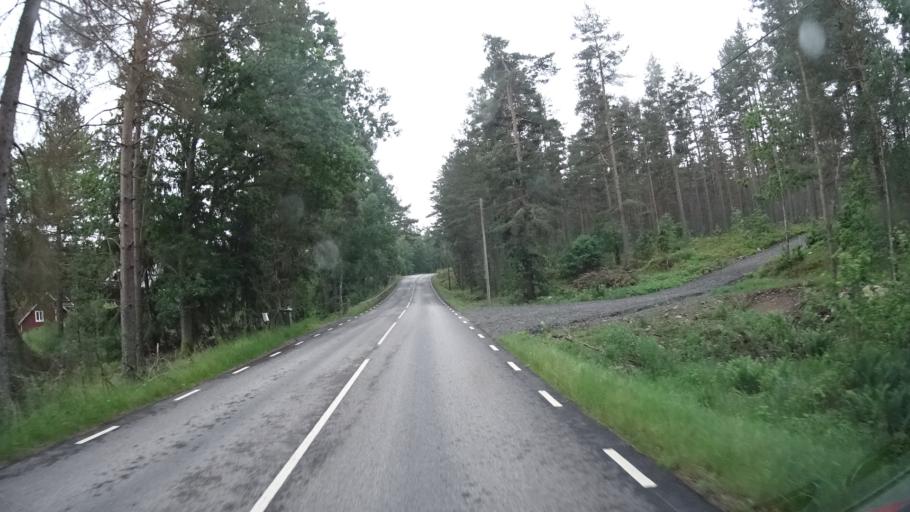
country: SE
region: Kalmar
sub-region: Oskarshamns Kommun
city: Oskarshamn
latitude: 57.3719
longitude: 16.2282
